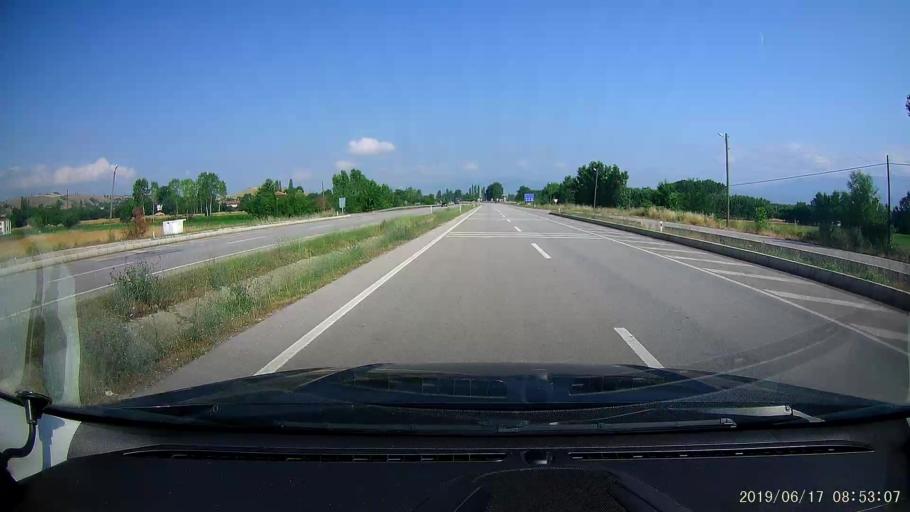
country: TR
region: Tokat
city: Erbaa
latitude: 40.7065
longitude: 36.4862
